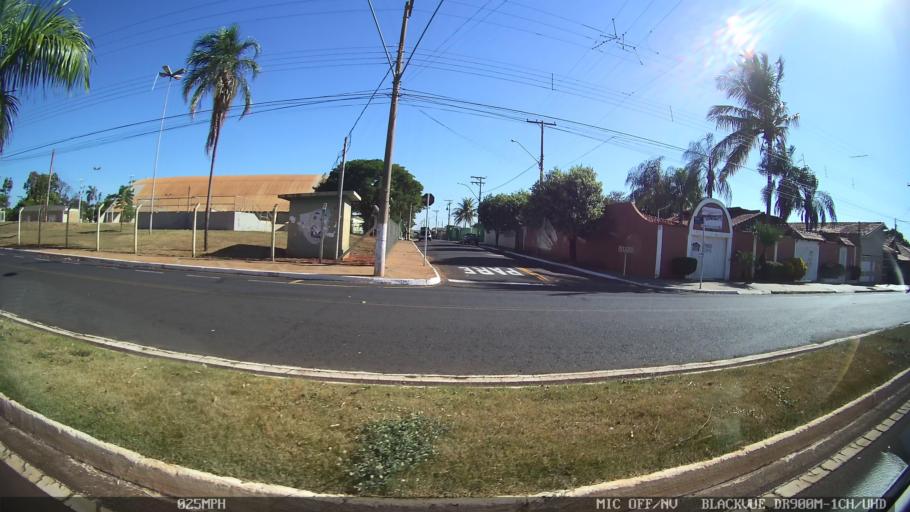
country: BR
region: Sao Paulo
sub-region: Olimpia
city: Olimpia
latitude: -20.7532
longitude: -48.9124
